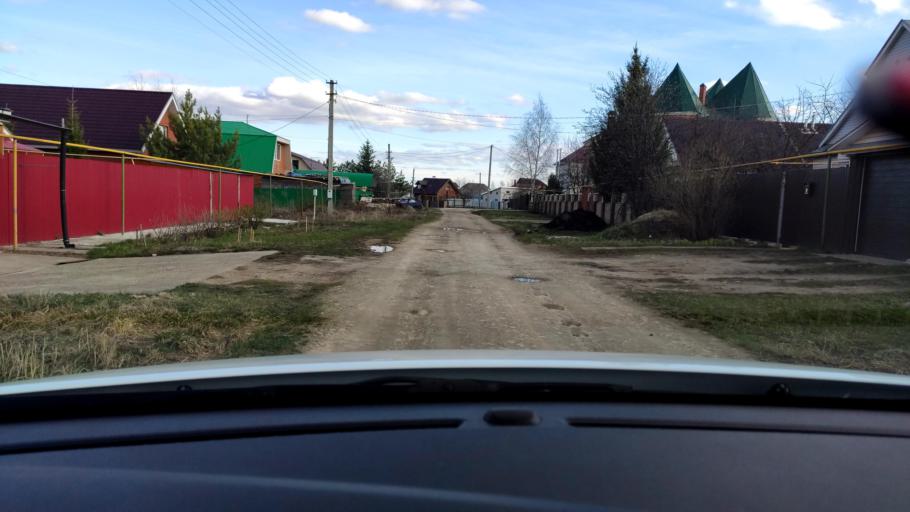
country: RU
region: Tatarstan
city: Vysokaya Gora
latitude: 55.8908
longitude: 49.3610
